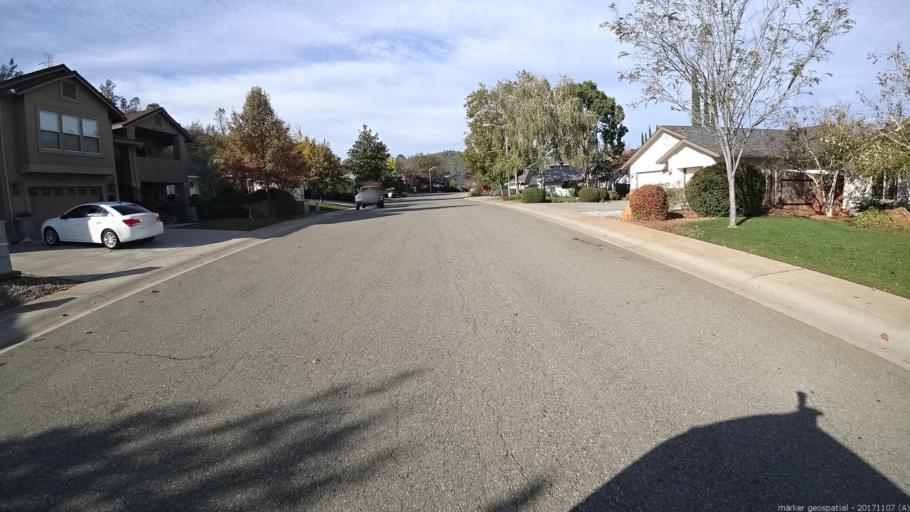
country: US
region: California
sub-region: Shasta County
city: Redding
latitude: 40.5673
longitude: -122.4357
